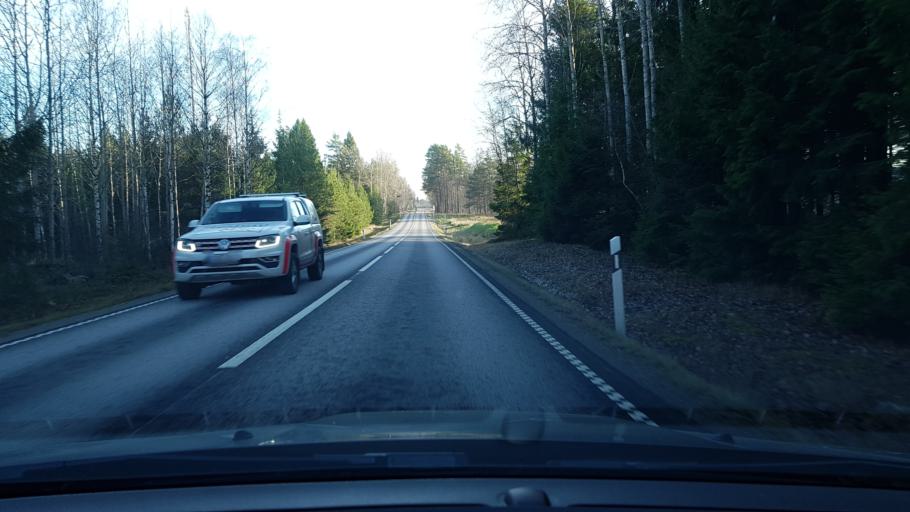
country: SE
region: Stockholm
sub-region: Norrtalje Kommun
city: Nykvarn
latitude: 59.7399
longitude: 18.2320
